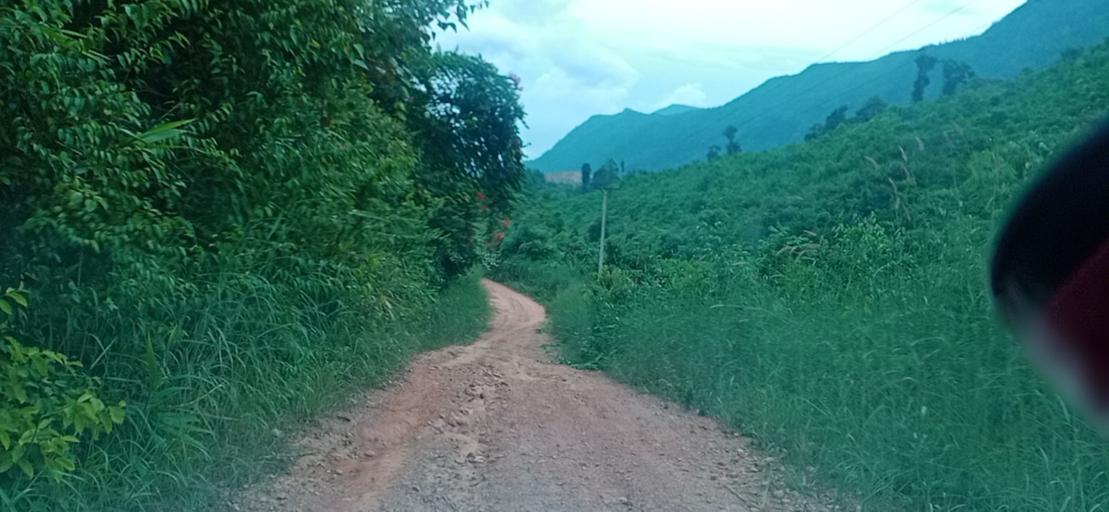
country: TH
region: Changwat Bueng Kan
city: Pak Khat
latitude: 18.5623
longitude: 103.2692
